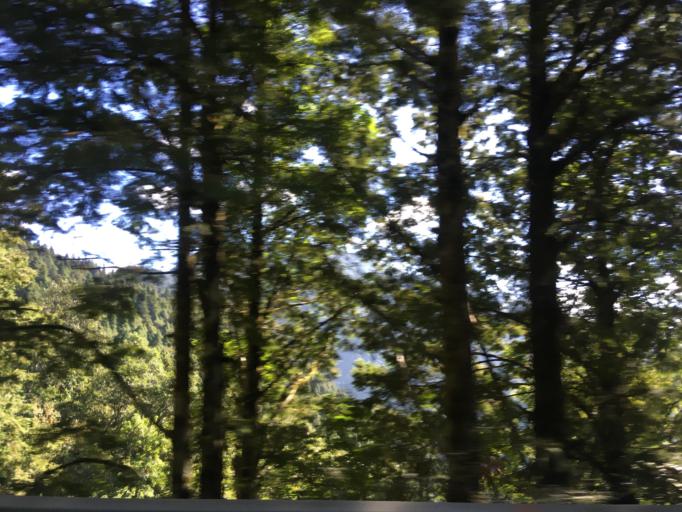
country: TW
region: Taiwan
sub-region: Yilan
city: Yilan
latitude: 24.4958
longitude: 121.5513
